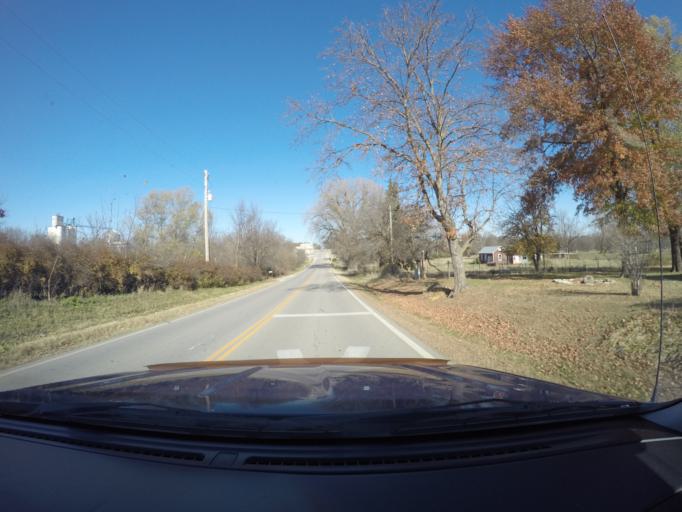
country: US
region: Kansas
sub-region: Marshall County
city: Marysville
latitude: 39.8571
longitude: -96.4170
